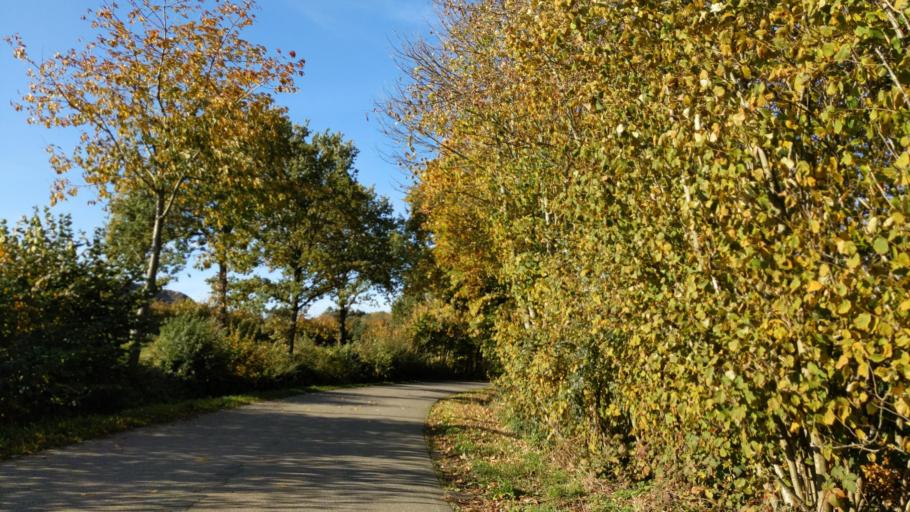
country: DE
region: Schleswig-Holstein
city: Kasseedorf
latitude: 54.1342
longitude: 10.7299
